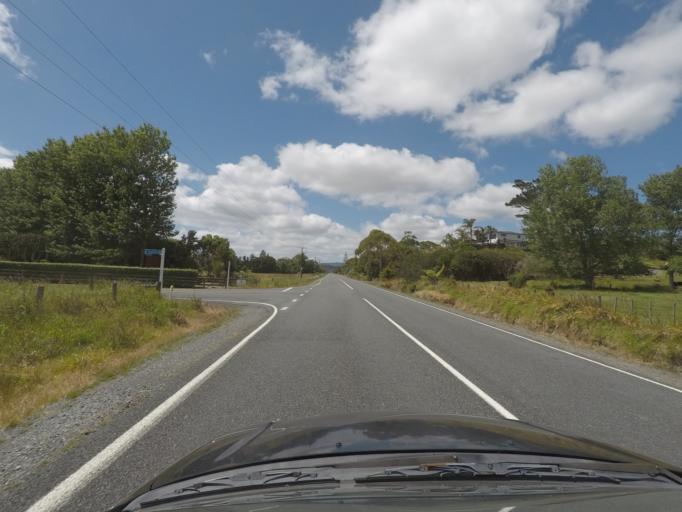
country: NZ
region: Northland
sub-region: Whangarei
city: Ruakaka
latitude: -35.9975
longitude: 174.4734
